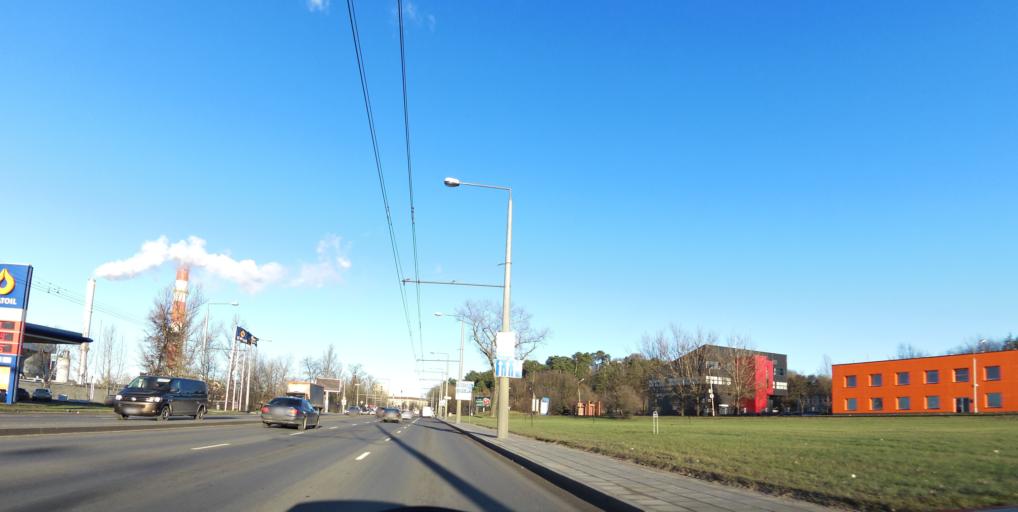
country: LT
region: Vilnius County
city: Vilkpede
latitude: 54.6623
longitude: 25.2352
